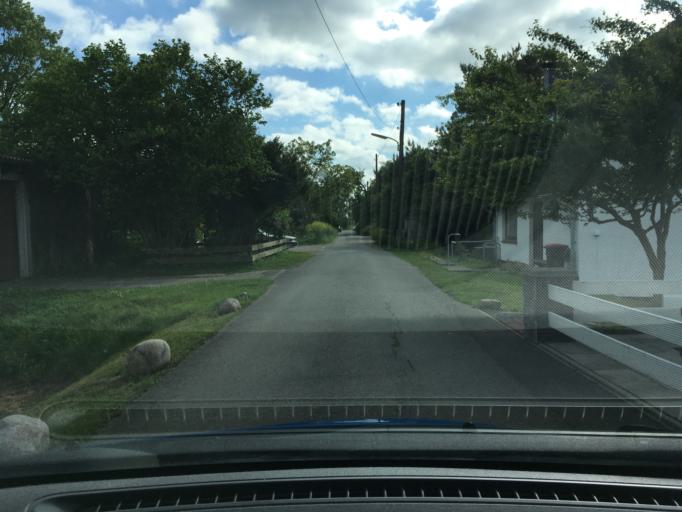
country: DE
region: Hamburg
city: Rothenburgsort
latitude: 53.4674
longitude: 10.0601
